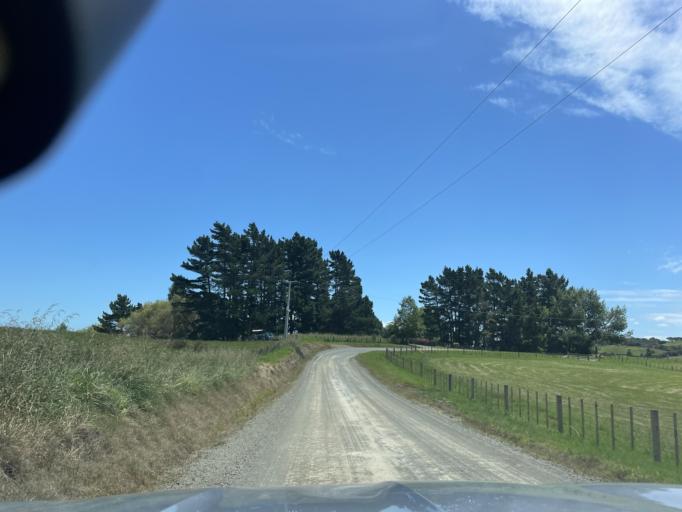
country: NZ
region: Auckland
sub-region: Auckland
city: Wellsford
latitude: -36.2249
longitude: 174.3662
